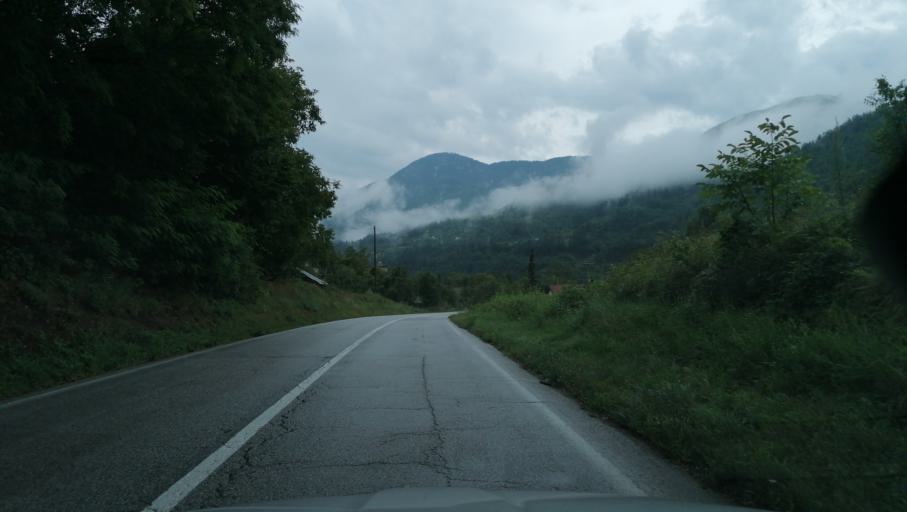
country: RS
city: Durici
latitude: 43.7609
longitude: 19.3860
